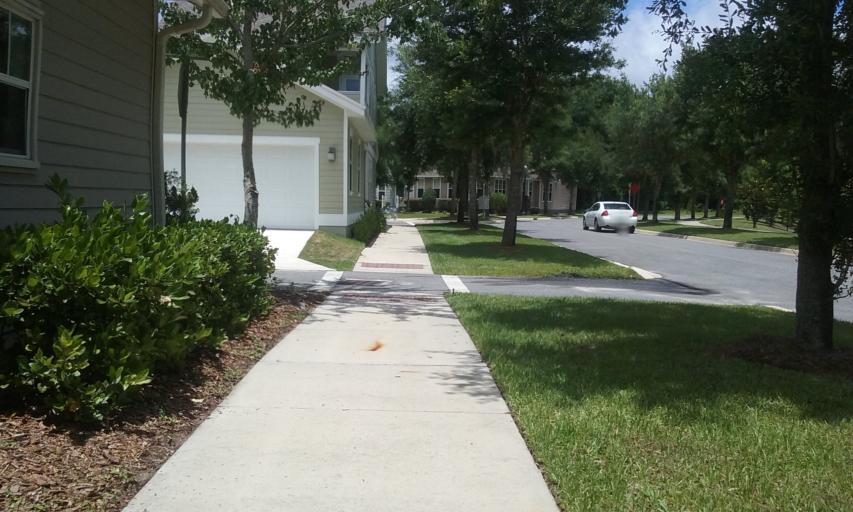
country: US
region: Florida
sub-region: Alachua County
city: Gainesville
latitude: 29.6833
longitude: -82.3574
